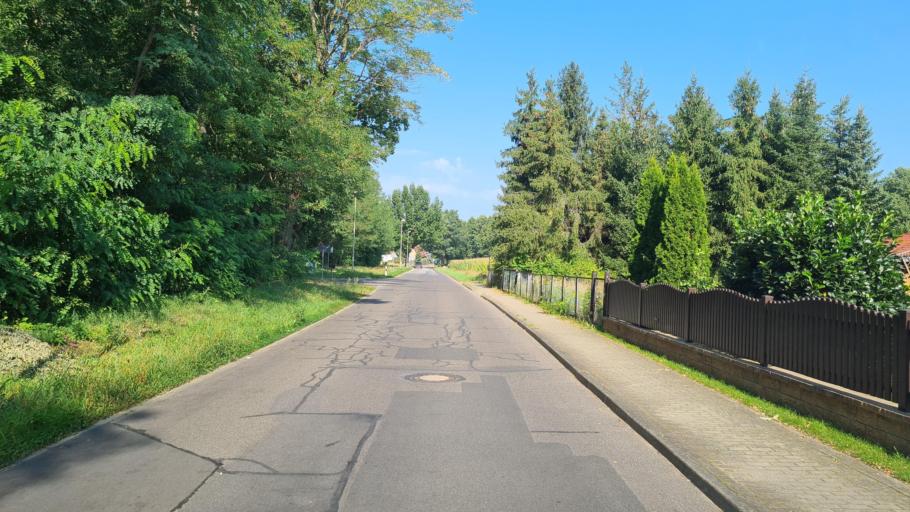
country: DE
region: Brandenburg
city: Kolkwitz
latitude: 51.7438
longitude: 14.2445
